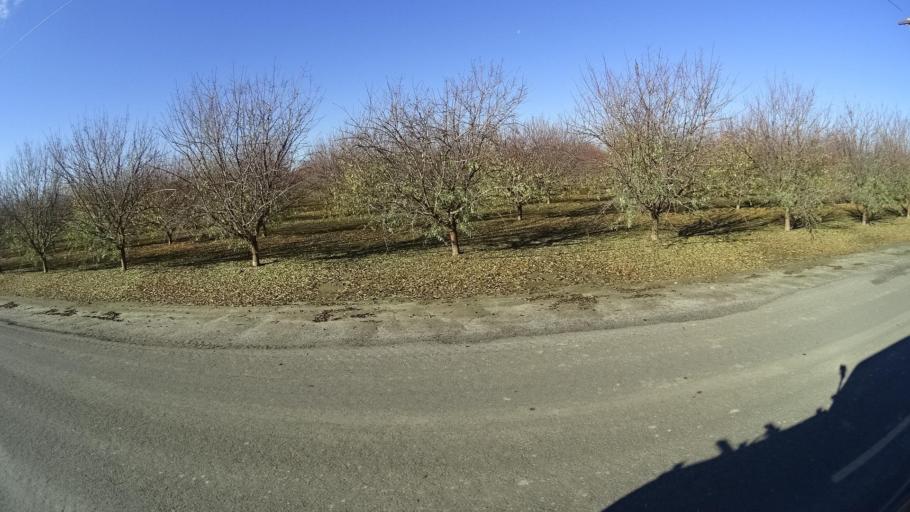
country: US
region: California
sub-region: Kern County
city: Delano
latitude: 35.7460
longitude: -119.3119
